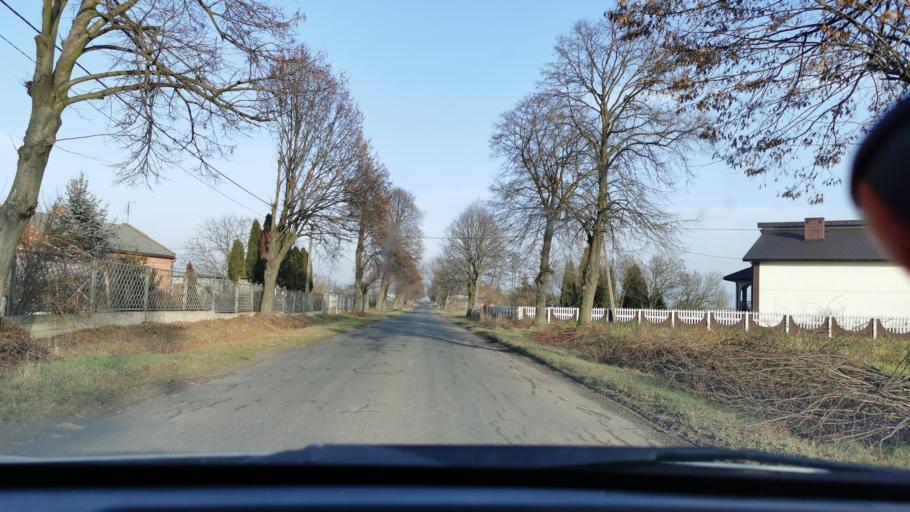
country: PL
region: Greater Poland Voivodeship
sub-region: Powiat kaliski
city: Opatowek
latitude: 51.6808
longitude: 18.3077
